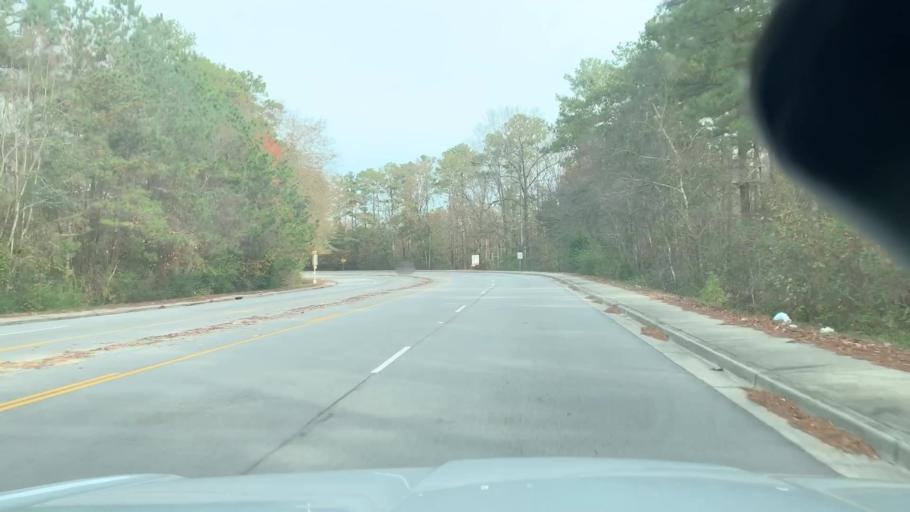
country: US
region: South Carolina
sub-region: Richland County
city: Dentsville
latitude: 34.0659
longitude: -80.9472
